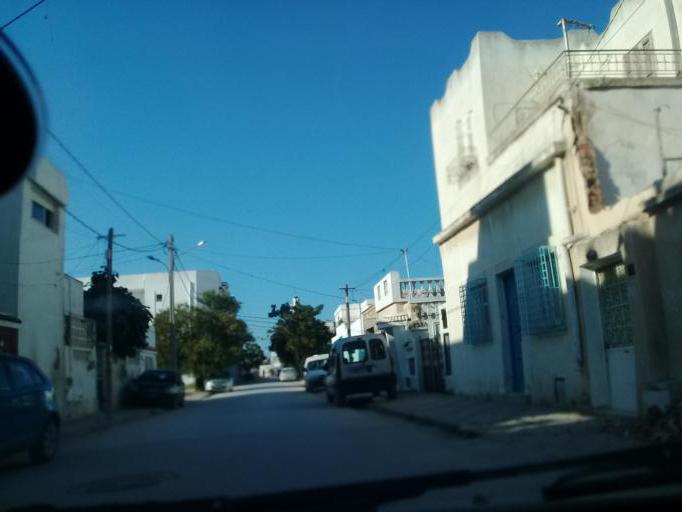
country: TN
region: Tunis
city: La Goulette
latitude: 36.8226
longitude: 10.3070
